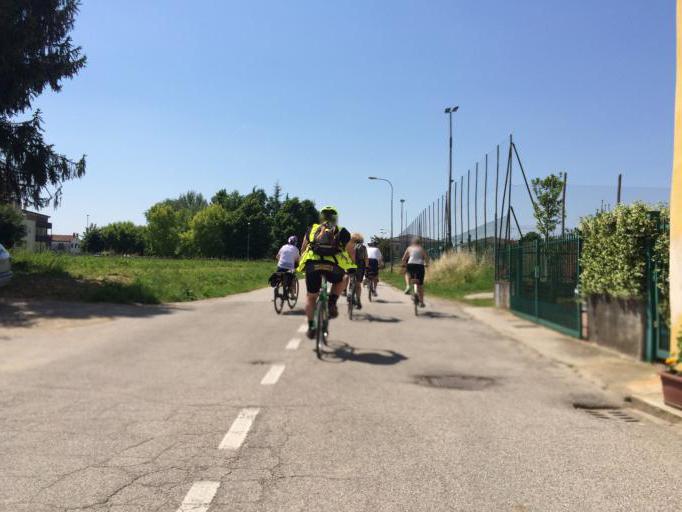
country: IT
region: Veneto
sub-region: Provincia di Vicenza
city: Villaganzerla
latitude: 45.4349
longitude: 11.6167
